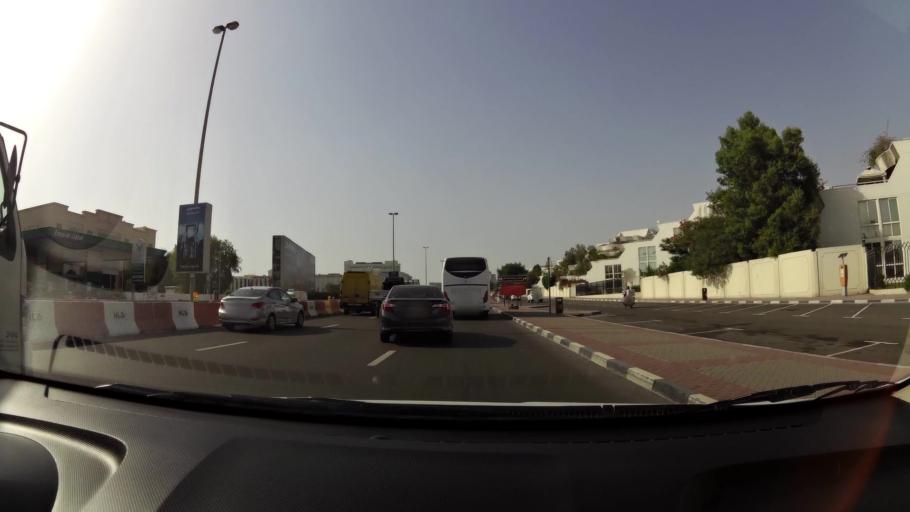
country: AE
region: Ash Shariqah
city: Sharjah
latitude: 25.2447
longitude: 55.3446
